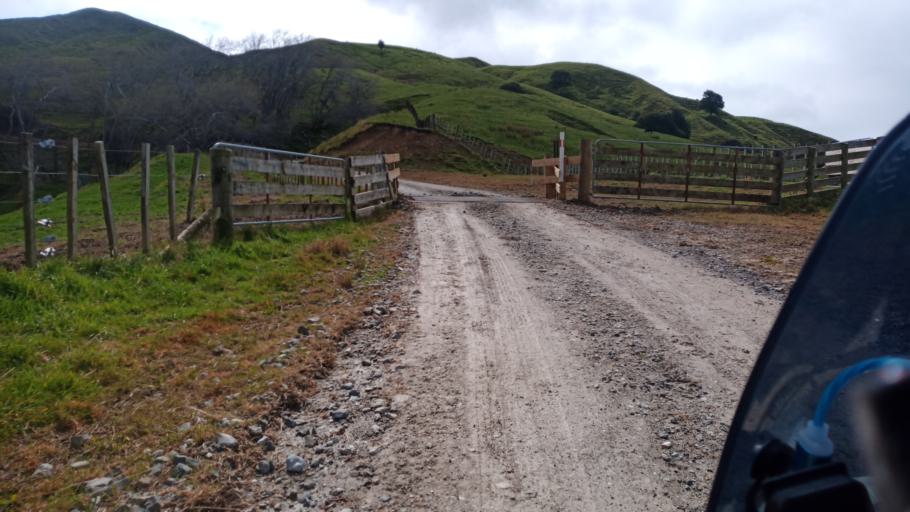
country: NZ
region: Gisborne
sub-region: Gisborne District
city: Gisborne
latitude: -38.5619
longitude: 178.1566
